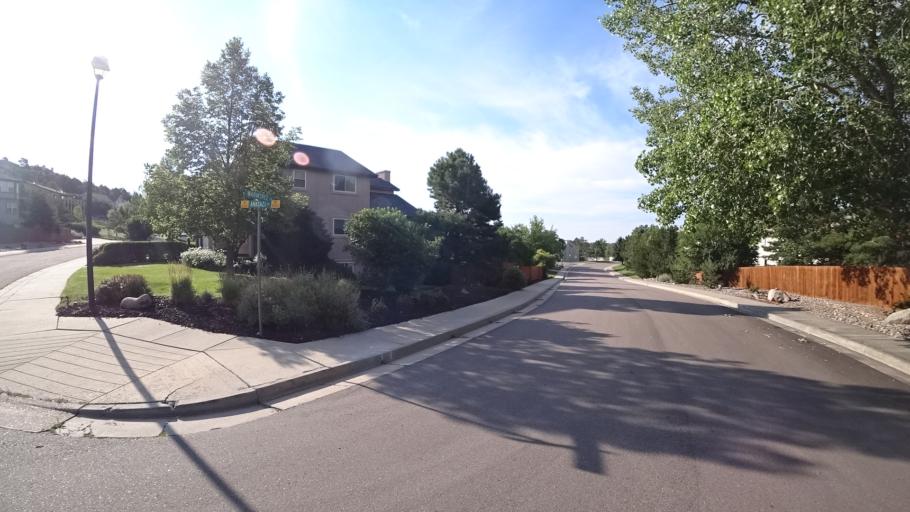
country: US
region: Colorado
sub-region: El Paso County
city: Air Force Academy
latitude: 38.9297
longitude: -104.8620
